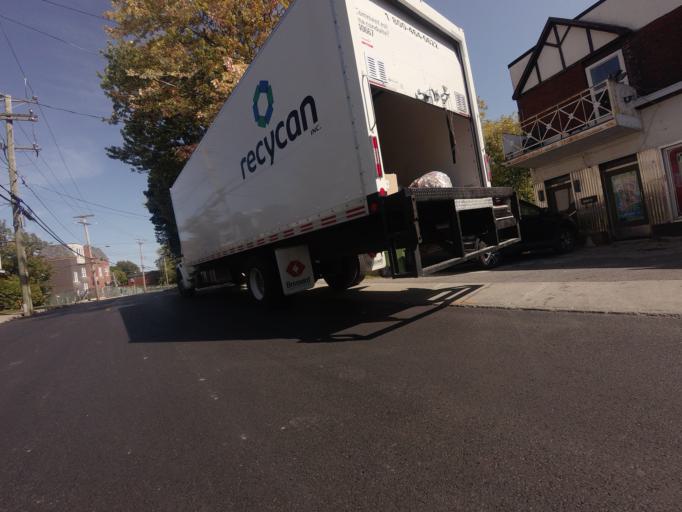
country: CA
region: Quebec
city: Kirkland
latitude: 45.4838
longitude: -73.8670
